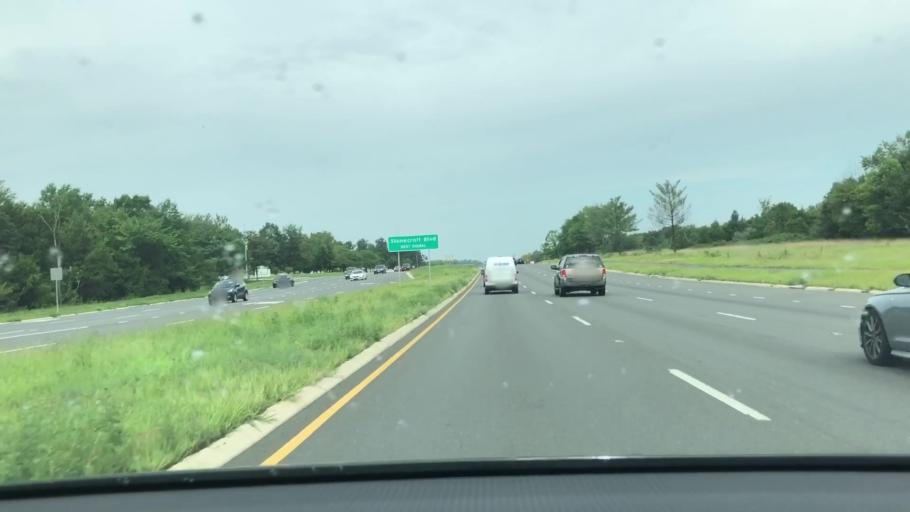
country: US
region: Virginia
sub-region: Fairfax County
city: Chantilly
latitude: 38.9025
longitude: -77.4515
